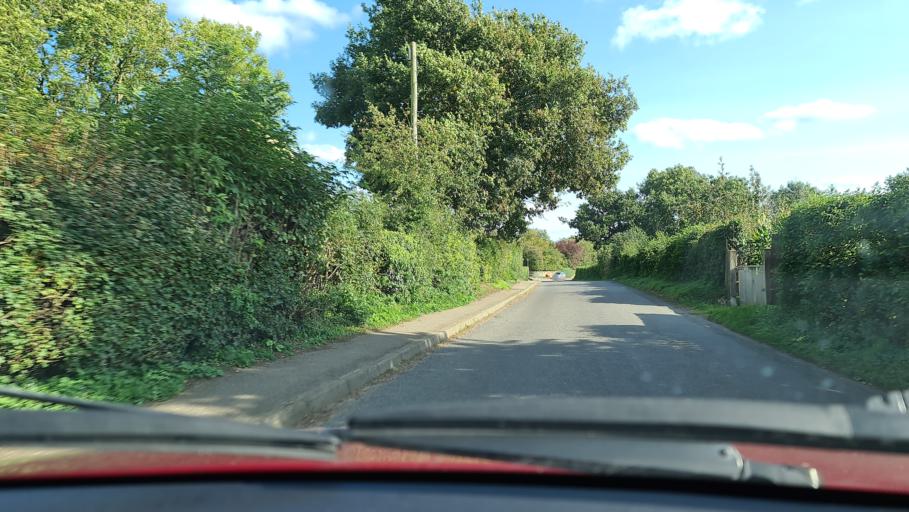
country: GB
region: England
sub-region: Oxfordshire
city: Adderbury
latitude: 52.0220
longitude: -1.2336
